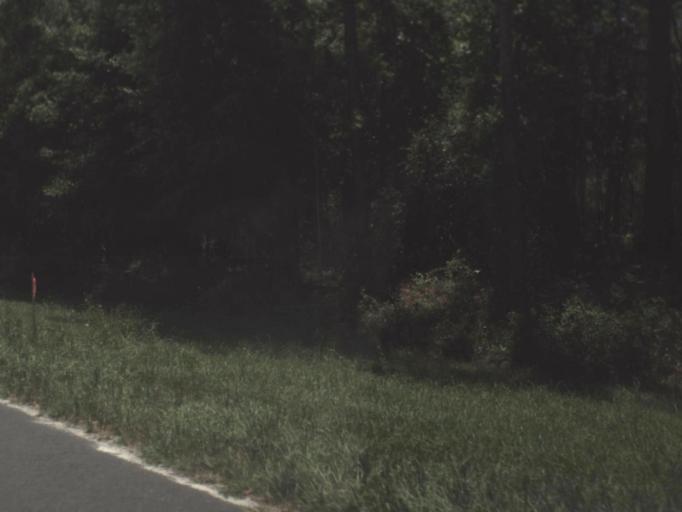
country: US
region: Florida
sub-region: Suwannee County
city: Live Oak
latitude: 30.3489
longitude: -83.1024
